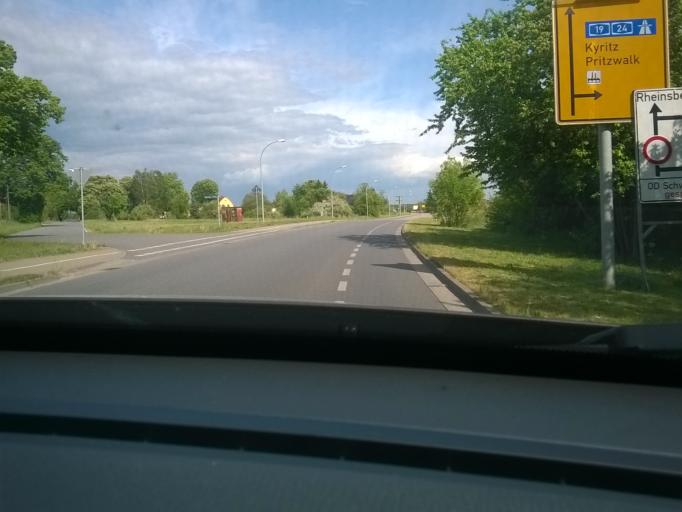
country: DE
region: Brandenburg
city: Wittstock
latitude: 53.1619
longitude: 12.5019
